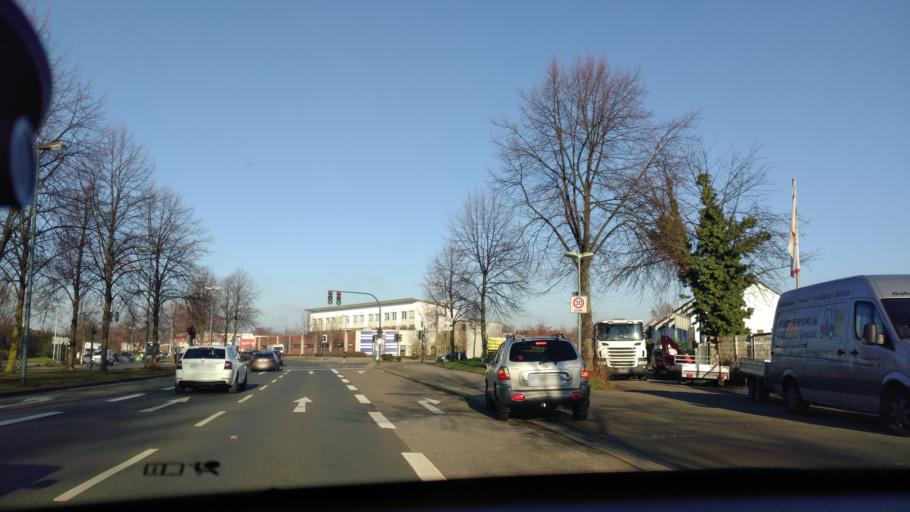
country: DE
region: North Rhine-Westphalia
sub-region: Regierungsbezirk Dusseldorf
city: Essen
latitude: 51.5014
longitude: 7.0097
